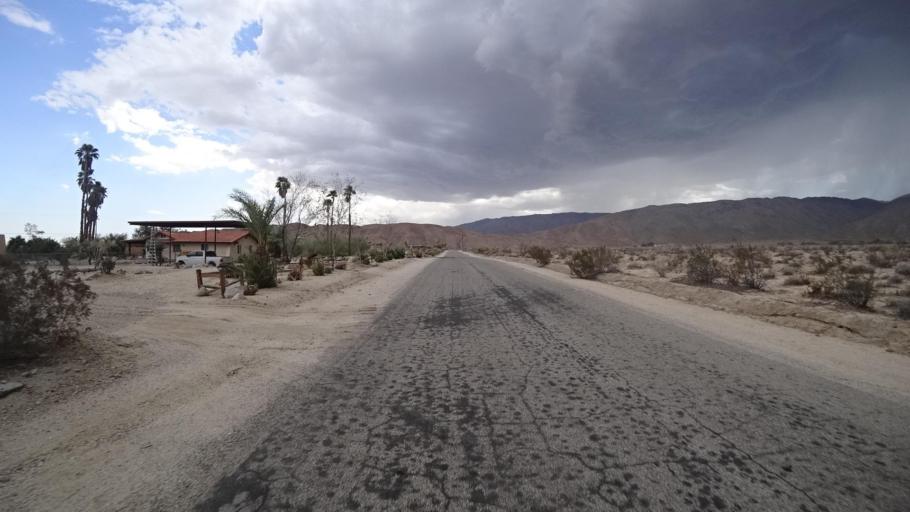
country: US
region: California
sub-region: San Diego County
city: Borrego Springs
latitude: 33.2615
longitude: -116.3995
